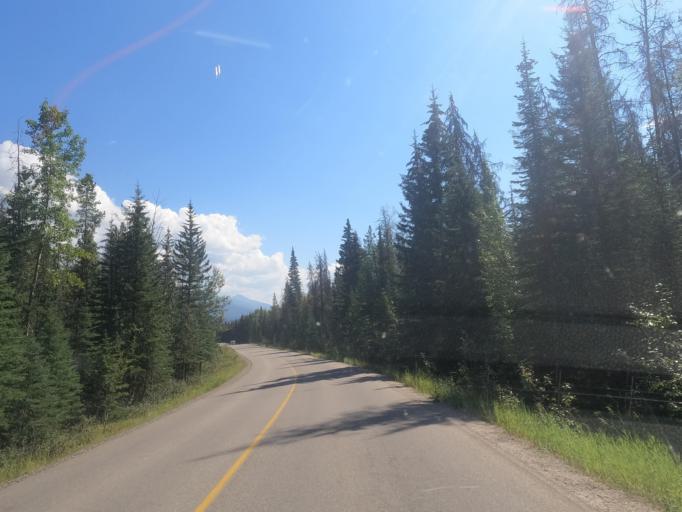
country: CA
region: Alberta
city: Jasper Park Lodge
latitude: 52.8560
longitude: -118.0946
